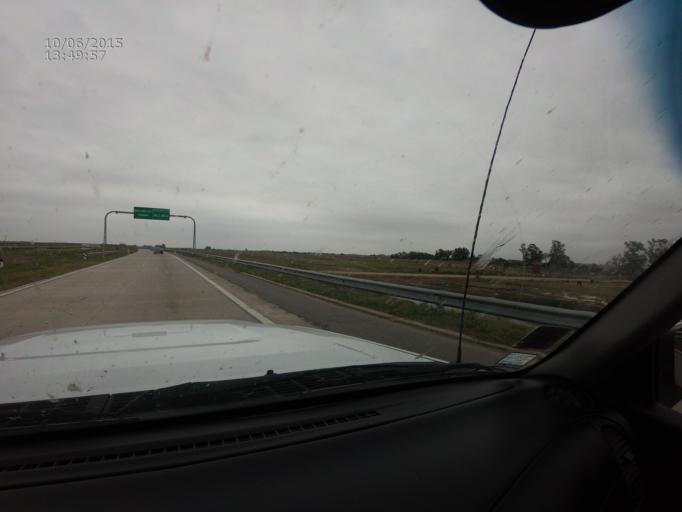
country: AR
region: Cordoba
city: Bell Ville
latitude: -32.5707
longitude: -62.6774
